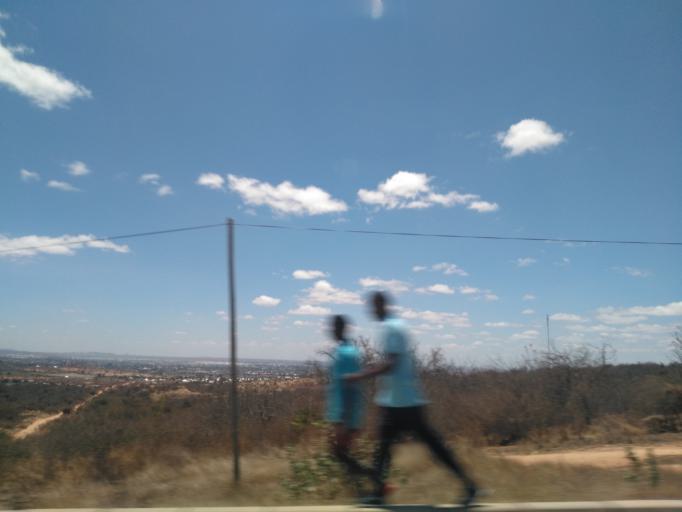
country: TZ
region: Dodoma
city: Kisasa
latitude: -6.2147
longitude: 35.7930
